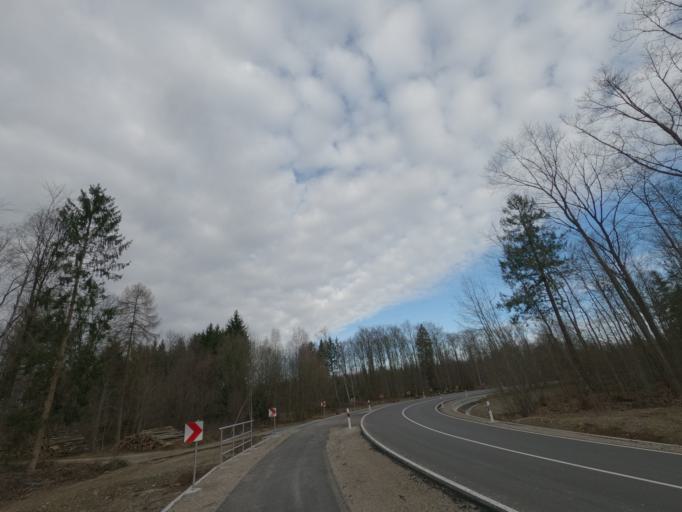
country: DE
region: Baden-Wuerttemberg
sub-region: Regierungsbezirk Stuttgart
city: Ohmden
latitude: 48.6547
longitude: 9.5277
